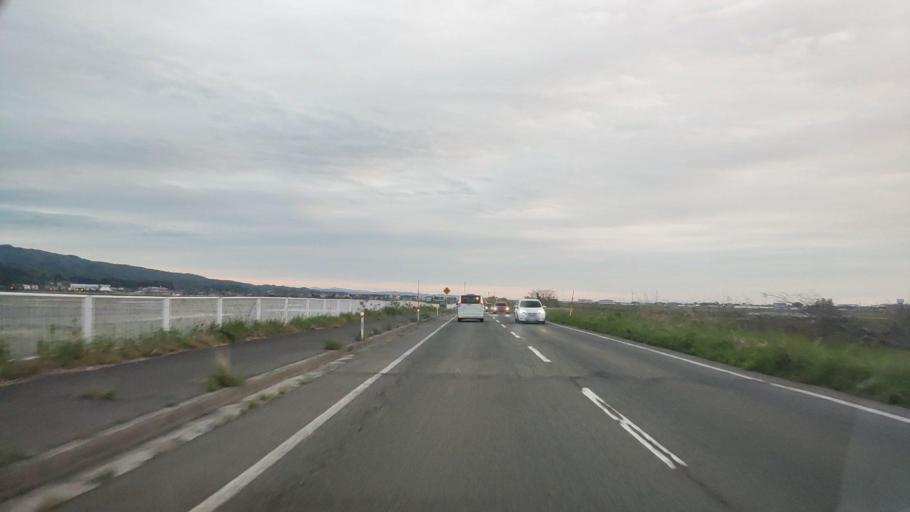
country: JP
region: Niigata
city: Niitsu-honcho
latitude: 37.7621
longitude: 139.0961
